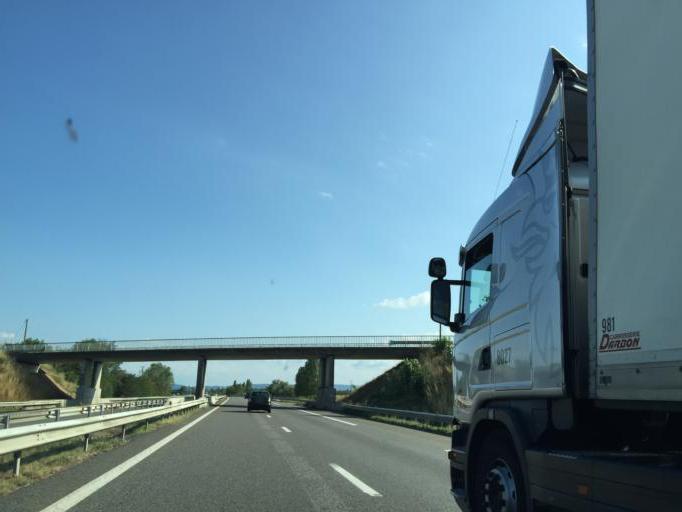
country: FR
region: Rhone-Alpes
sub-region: Departement de la Loire
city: Cuzieu
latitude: 45.5922
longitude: 4.2110
